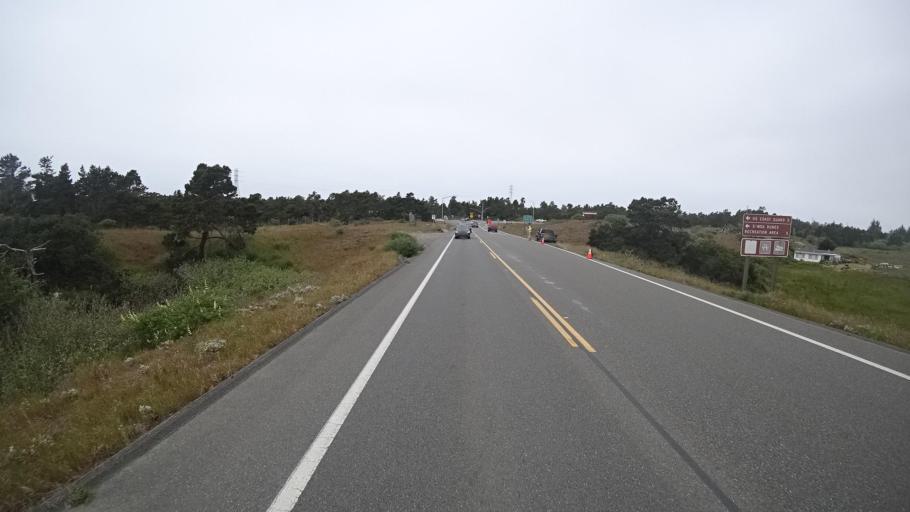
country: US
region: California
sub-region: Humboldt County
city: Eureka
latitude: 40.8249
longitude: -124.1749
